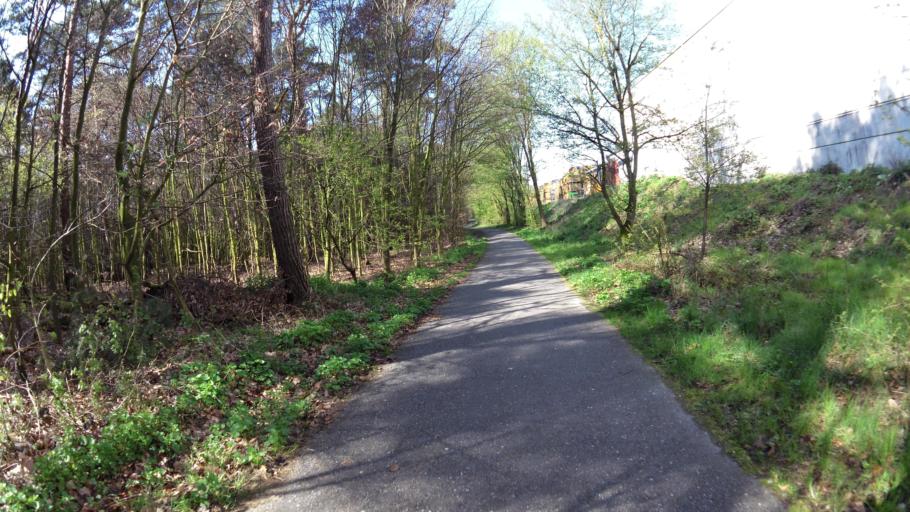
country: DE
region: North Rhine-Westphalia
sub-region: Regierungsbezirk Koln
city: Gangelt
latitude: 50.9858
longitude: 5.9876
